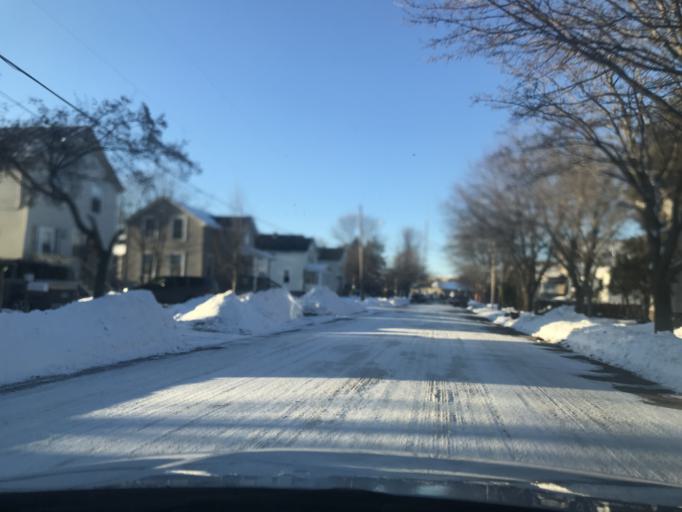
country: US
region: Michigan
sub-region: Menominee County
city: Menominee
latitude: 45.1050
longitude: -87.6046
